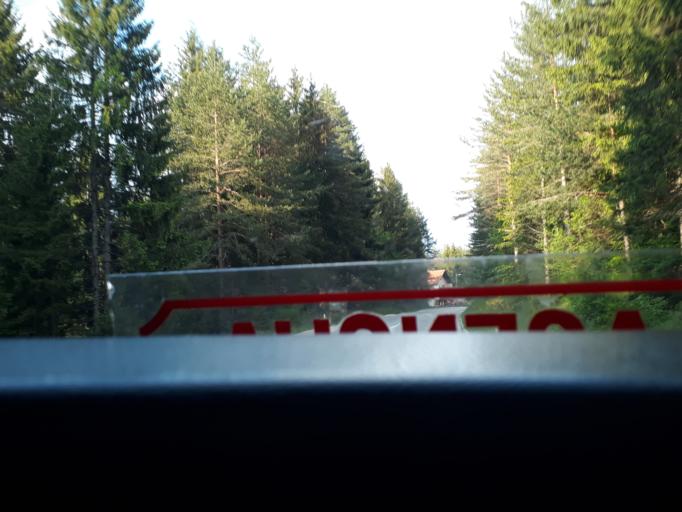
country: BA
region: Federation of Bosnia and Herzegovina
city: Olovo
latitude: 44.0656
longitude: 18.4869
